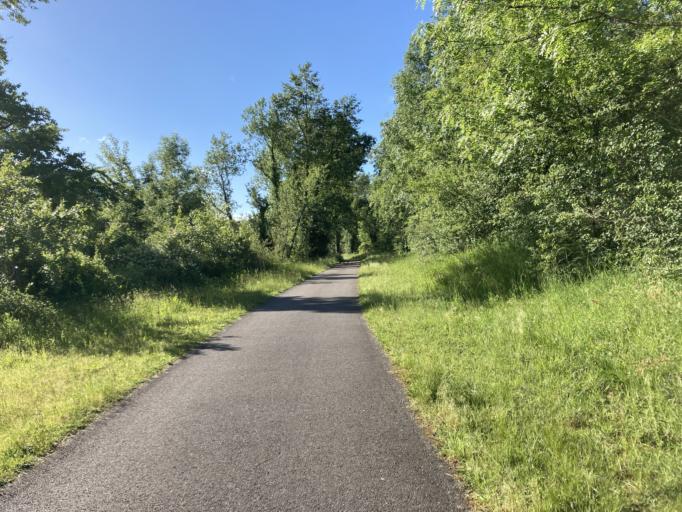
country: FR
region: Aquitaine
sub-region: Departement des Pyrenees-Atlantiques
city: Artiguelouve
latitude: 43.3258
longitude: -0.4591
